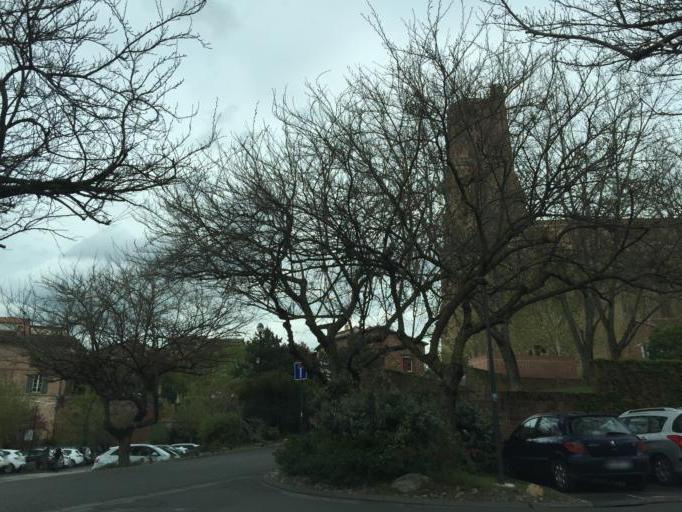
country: FR
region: Midi-Pyrenees
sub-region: Departement du Tarn
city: Albi
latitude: 43.9273
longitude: 2.1417
